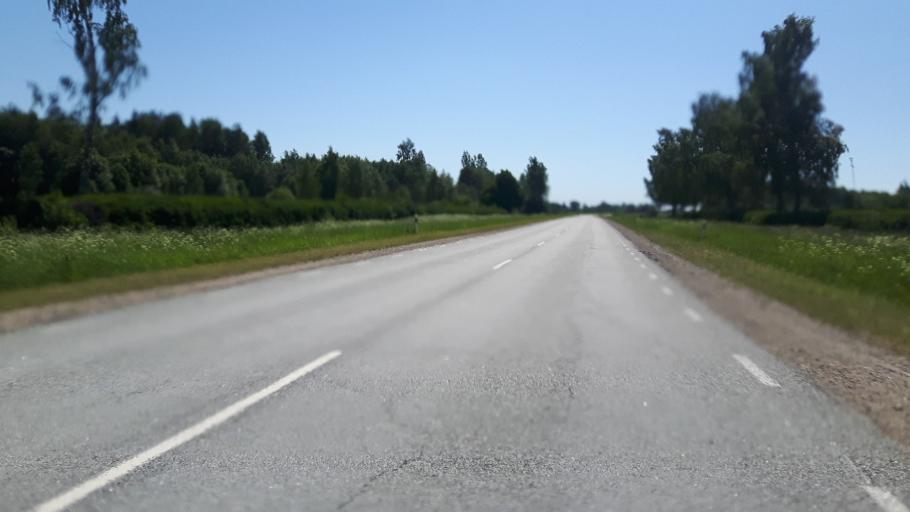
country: EE
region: Paernumaa
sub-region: Tootsi vald
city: Tootsi
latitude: 58.4573
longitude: 24.7794
